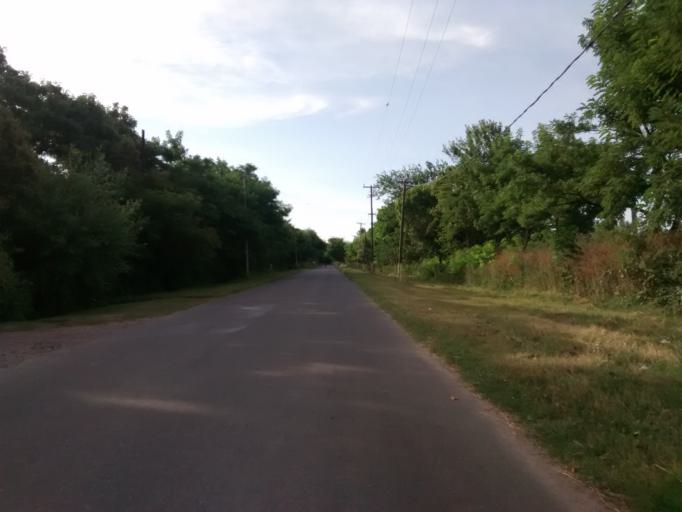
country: AR
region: Buenos Aires
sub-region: Partido de La Plata
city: La Plata
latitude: -34.8402
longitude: -58.0907
